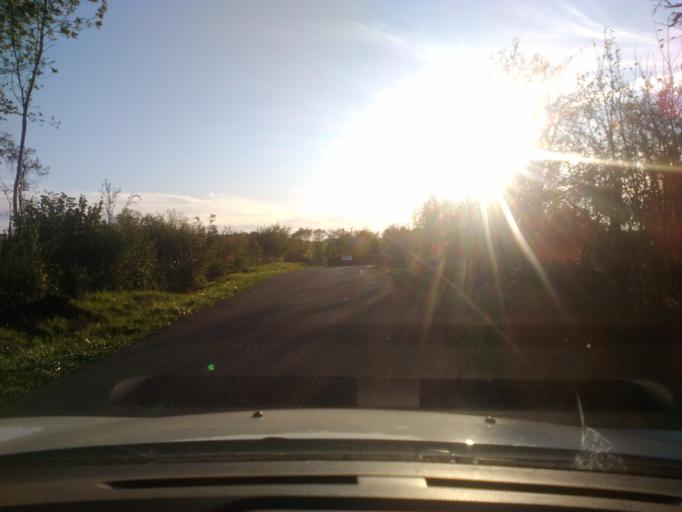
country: FR
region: Lorraine
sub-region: Departement des Vosges
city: Vincey
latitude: 48.3292
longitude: 6.3093
